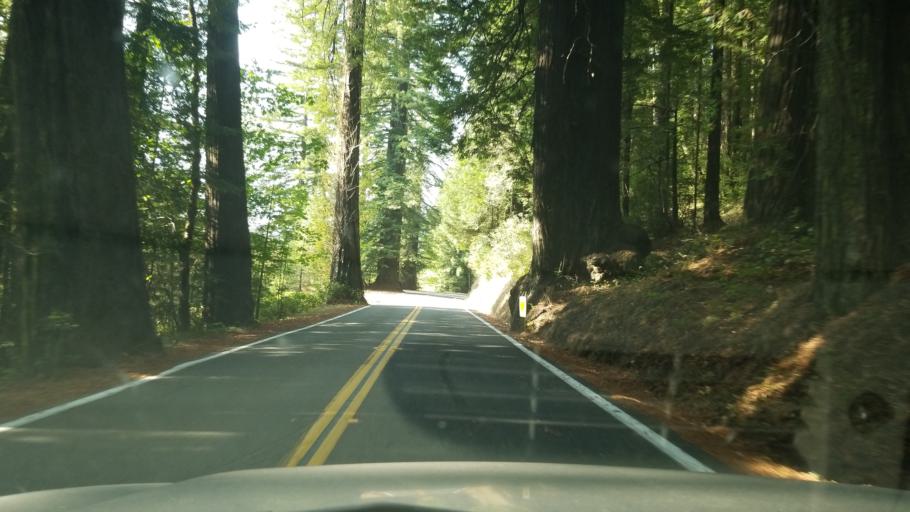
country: US
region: California
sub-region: Humboldt County
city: Redway
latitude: 40.2454
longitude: -123.8219
